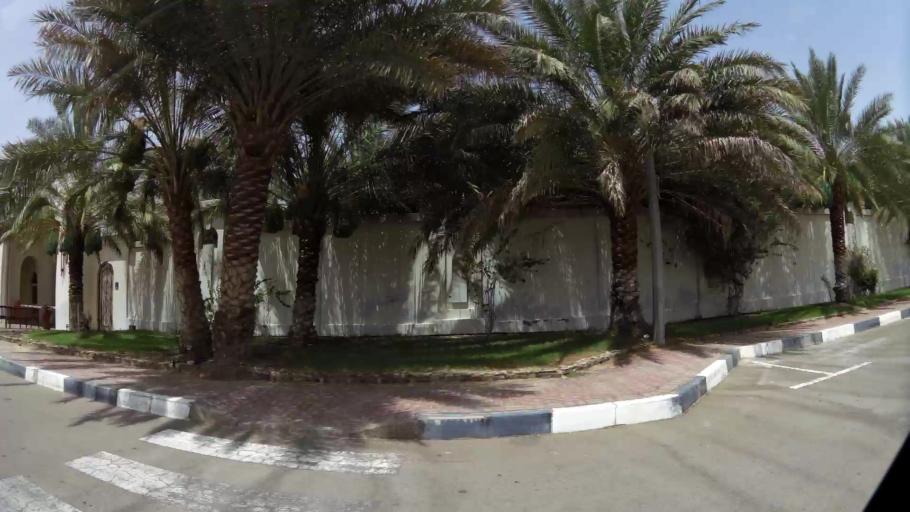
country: AE
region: Abu Dhabi
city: Al Ain
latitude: 24.1864
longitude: 55.6790
